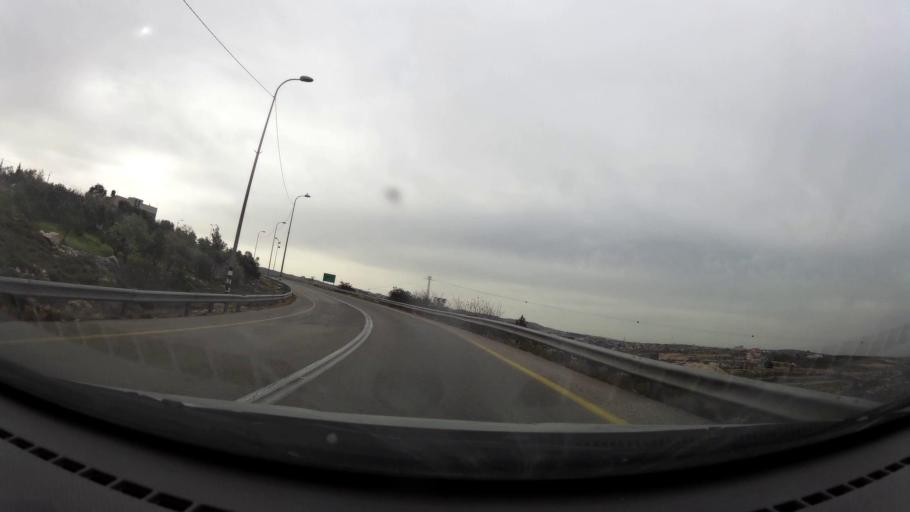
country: PS
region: West Bank
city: Surif
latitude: 31.6706
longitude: 35.0732
